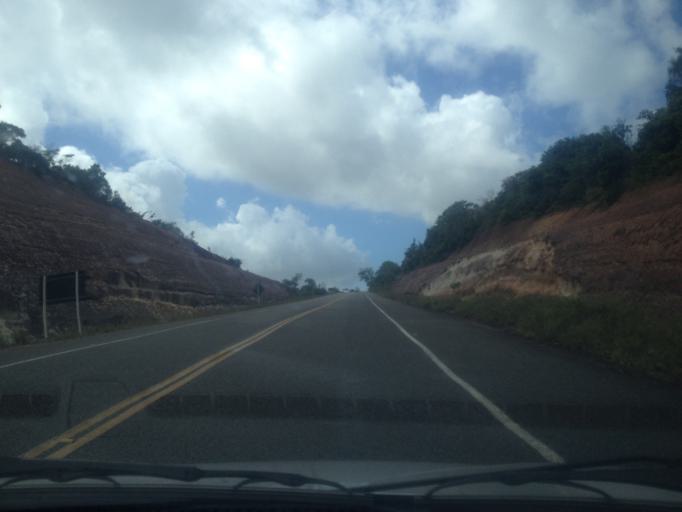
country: BR
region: Bahia
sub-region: Conde
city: Conde
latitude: -12.0846
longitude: -37.7716
